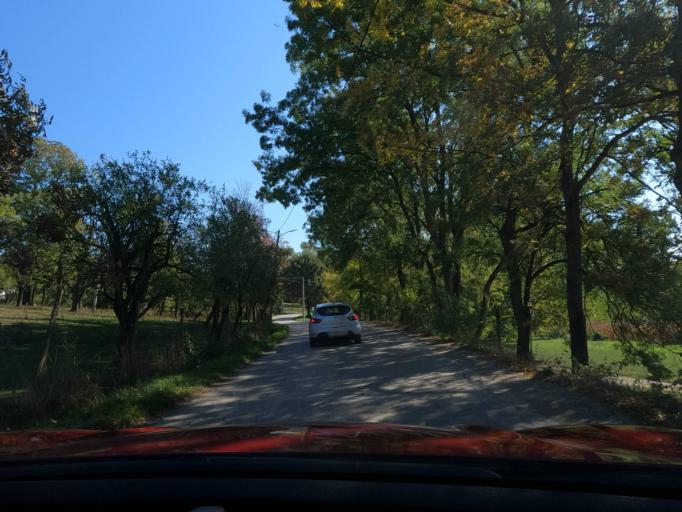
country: RS
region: Central Serbia
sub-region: Raski Okrug
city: Kraljevo
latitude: 43.7718
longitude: 20.6571
